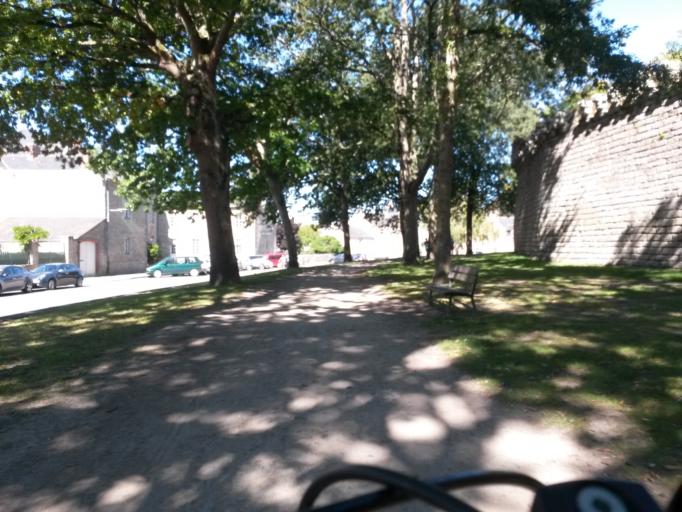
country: FR
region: Pays de la Loire
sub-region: Departement de la Loire-Atlantique
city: Guerande
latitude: 47.3265
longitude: -2.4318
